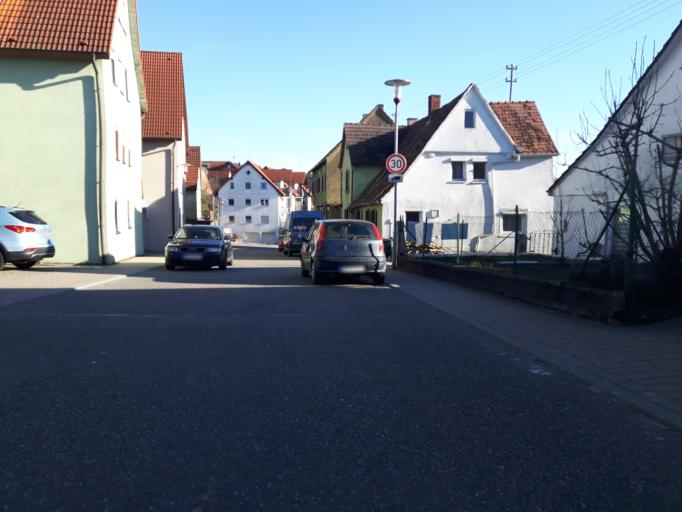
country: DE
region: Baden-Wuerttemberg
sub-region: Regierungsbezirk Stuttgart
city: Massenbachhausen
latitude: 49.1784
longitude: 9.0449
